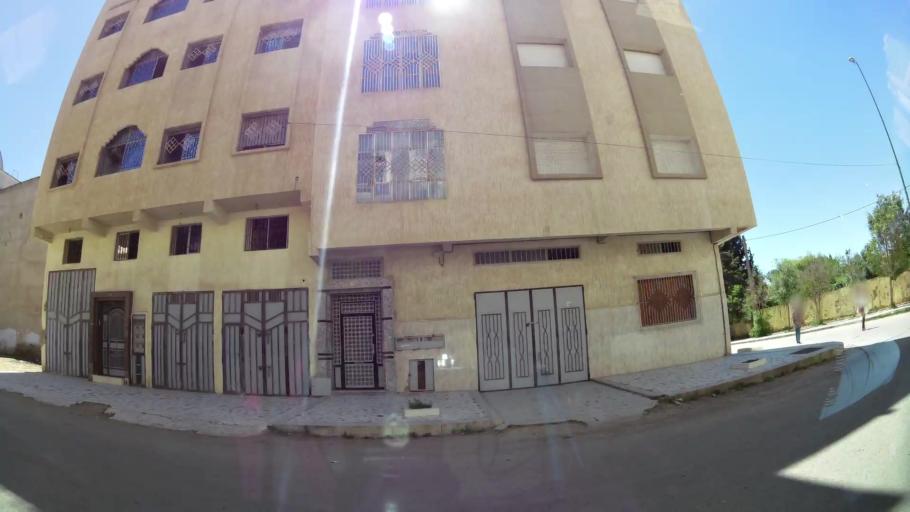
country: MA
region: Meknes-Tafilalet
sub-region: Meknes
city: Meknes
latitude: 33.8954
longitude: -5.5831
